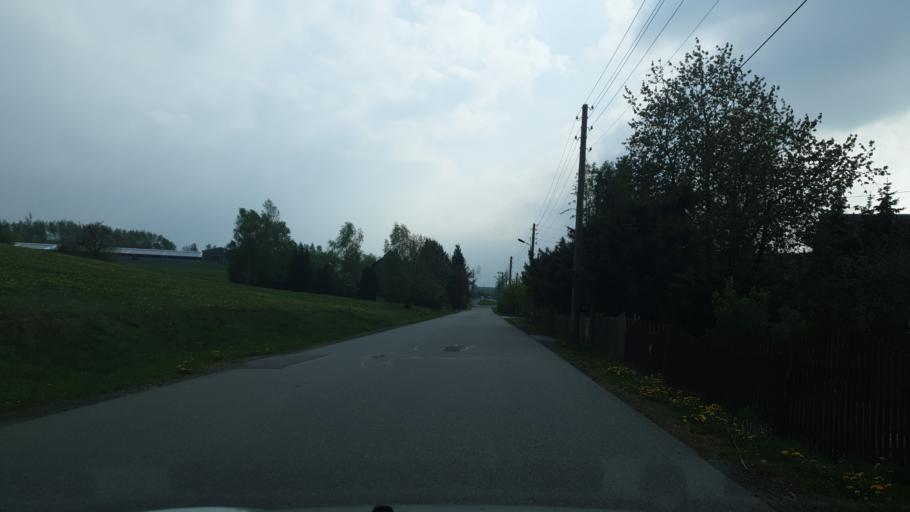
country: DE
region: Saxony
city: Stollberg
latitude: 50.6945
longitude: 12.7704
